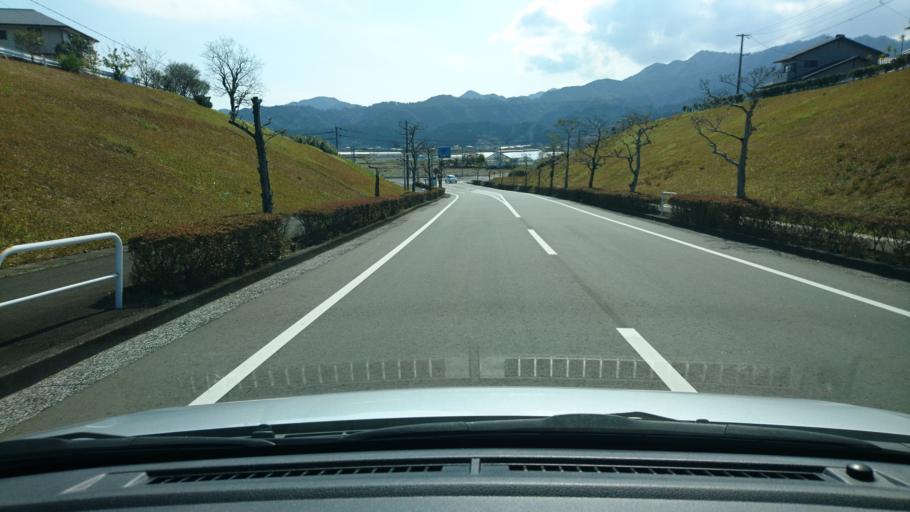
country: JP
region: Miyazaki
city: Miyazaki-shi
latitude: 31.8265
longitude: 131.4266
